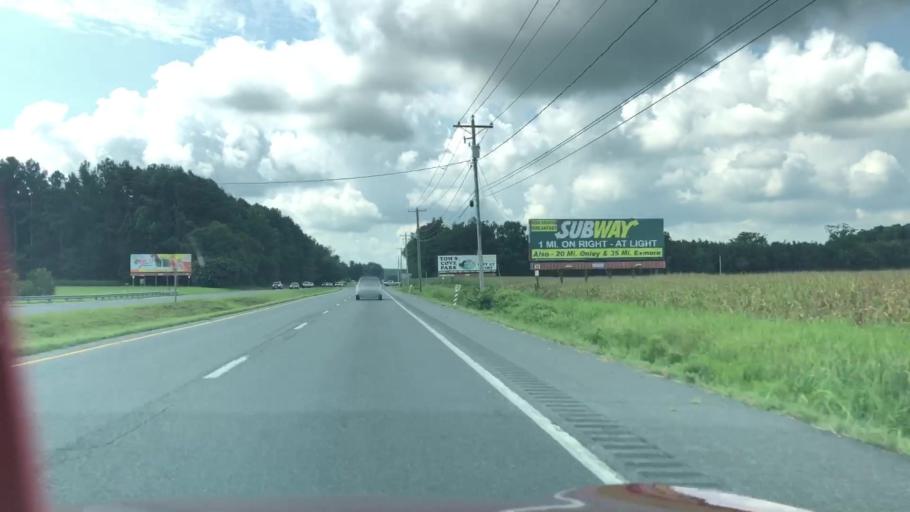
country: US
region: Virginia
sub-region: Accomack County
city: Wattsville
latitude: 37.9664
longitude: -75.5327
